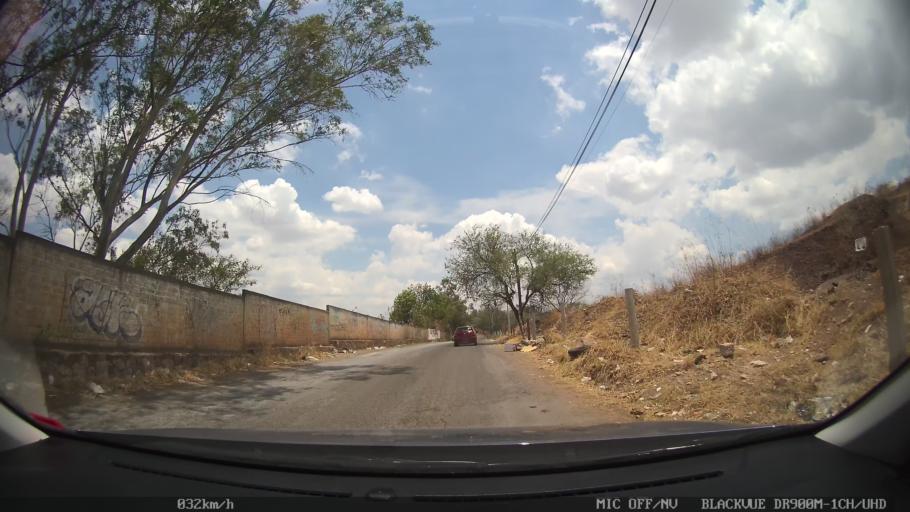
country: MX
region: Jalisco
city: Tonala
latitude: 20.6306
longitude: -103.2227
